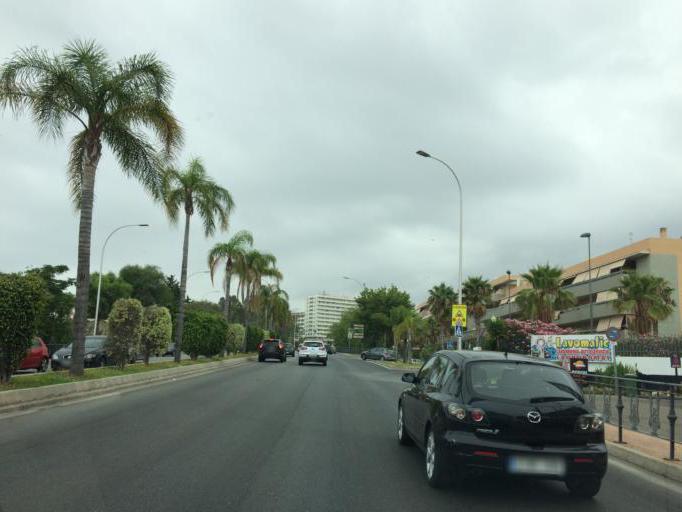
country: ES
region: Andalusia
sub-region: Provincia de Malaga
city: Torremolinos
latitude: 36.6413
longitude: -4.4947
